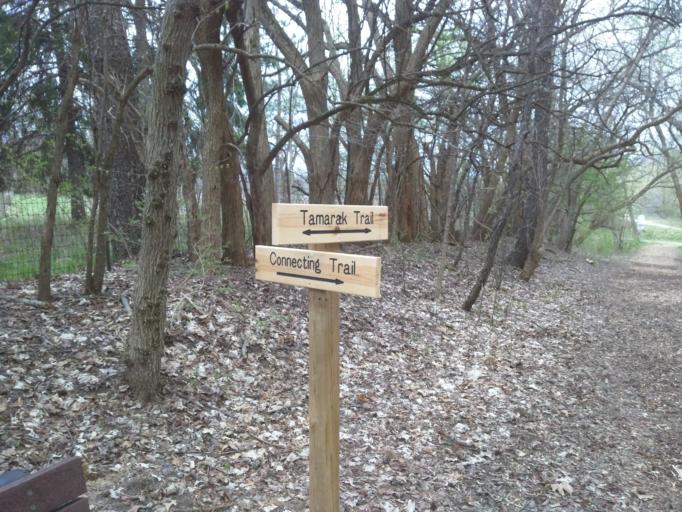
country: US
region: Michigan
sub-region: Ingham County
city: East Lansing
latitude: 42.7065
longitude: -84.5178
